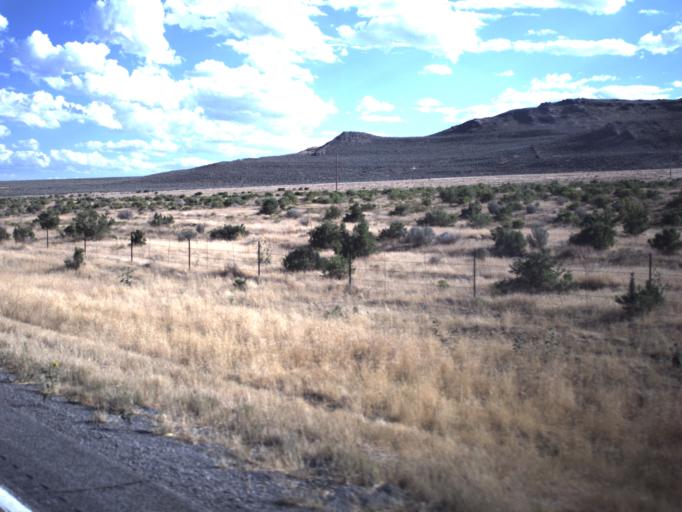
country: US
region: Utah
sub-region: Tooele County
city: Grantsville
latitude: 40.6450
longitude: -112.5275
